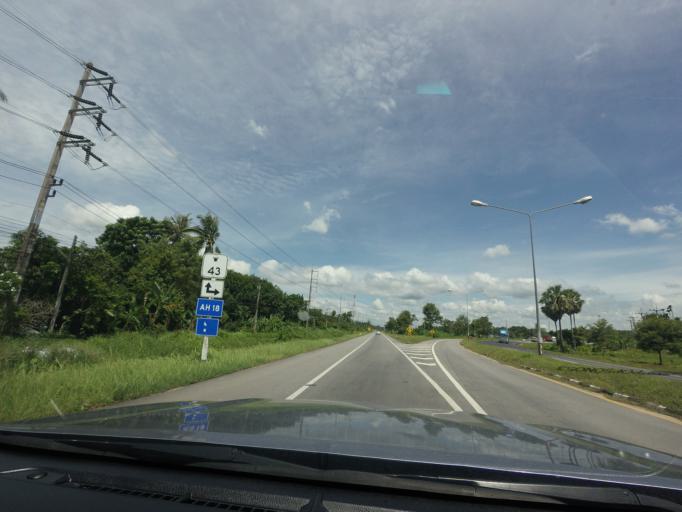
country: TH
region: Songkhla
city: Chana
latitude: 6.9831
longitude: 100.6805
